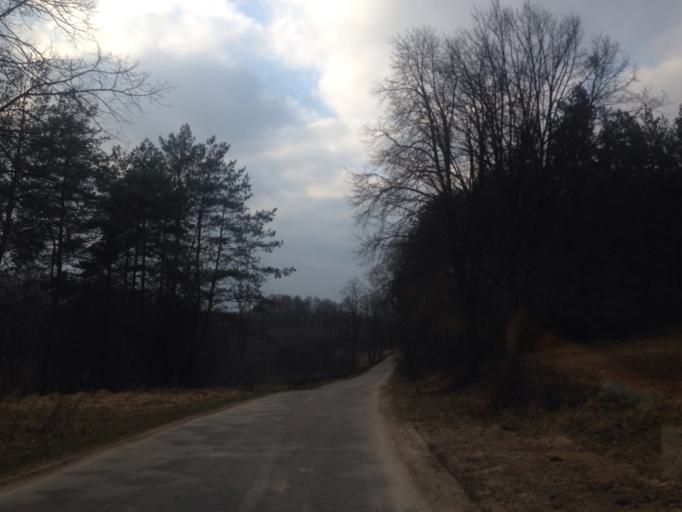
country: PL
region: Warmian-Masurian Voivodeship
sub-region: Powiat dzialdowski
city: Lidzbark
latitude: 53.3480
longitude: 19.7325
